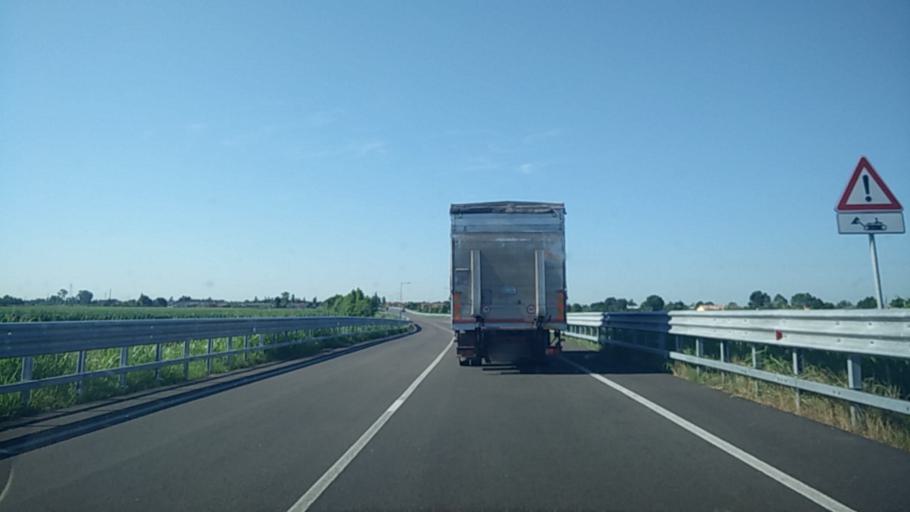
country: IT
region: Veneto
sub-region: Provincia di Venezia
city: Cazzago-Ex Polo
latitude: 45.4403
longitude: 12.0900
